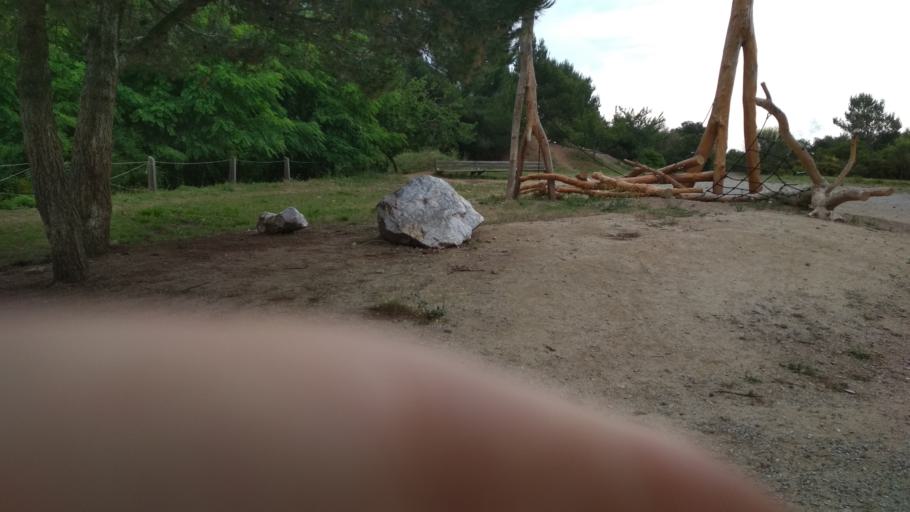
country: ES
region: Catalonia
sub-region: Provincia de Barcelona
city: Nou Barris
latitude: 41.4478
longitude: 2.1366
